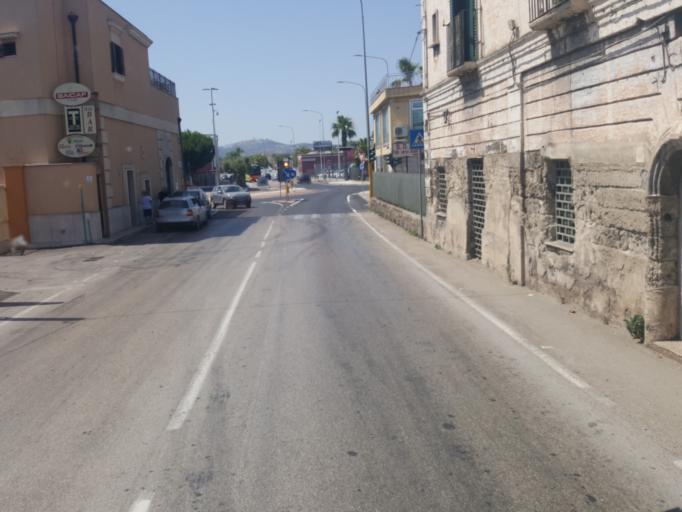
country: IT
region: Apulia
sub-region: Provincia di Taranto
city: Massafra
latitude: 40.5854
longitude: 17.1086
